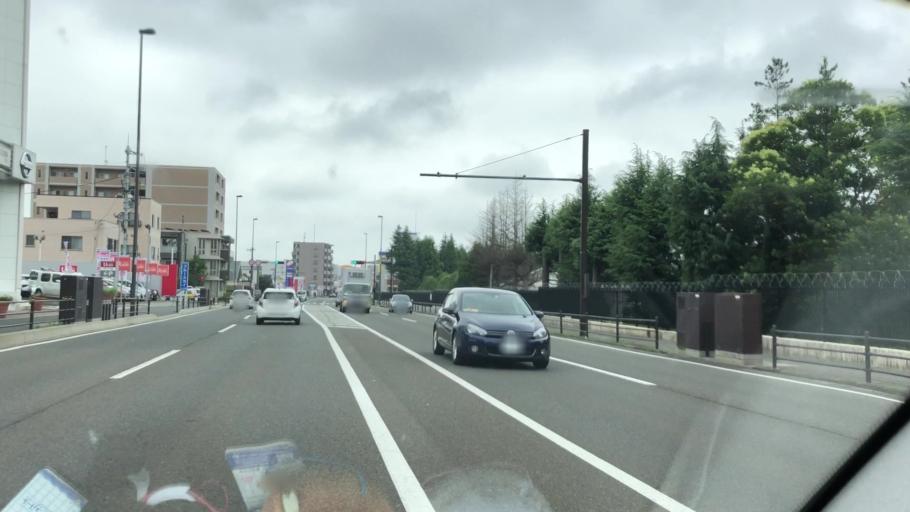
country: JP
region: Miyagi
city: Sendai-shi
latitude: 38.2693
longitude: 140.9211
